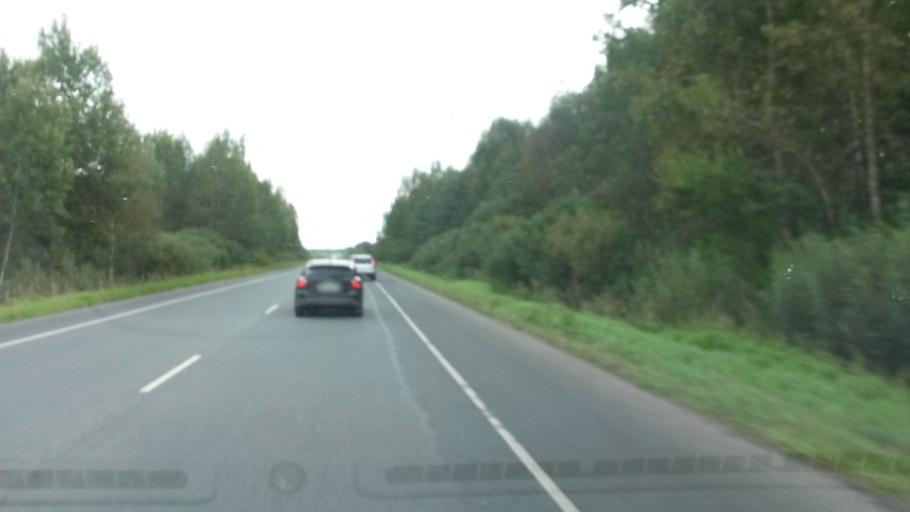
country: RU
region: Ivanovo
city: Rodniki
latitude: 57.0869
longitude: 41.6261
